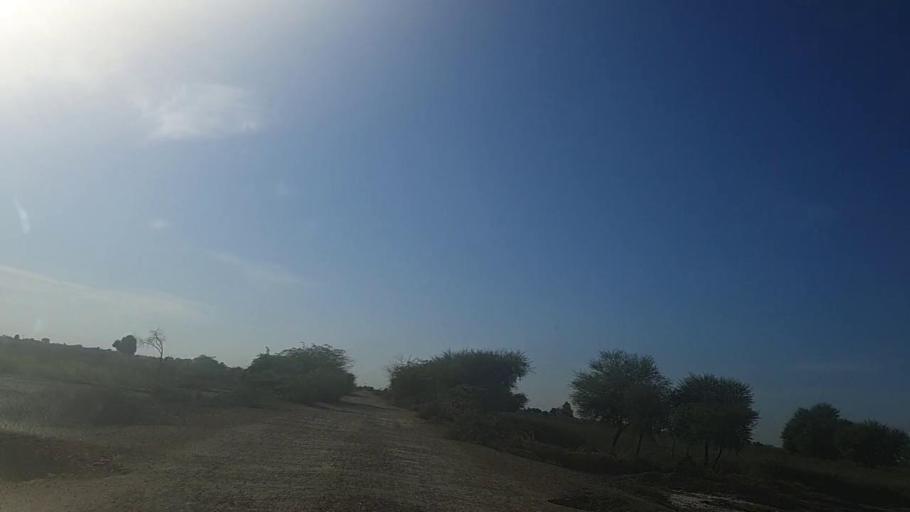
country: PK
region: Sindh
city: Pithoro
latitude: 25.5219
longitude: 69.3800
